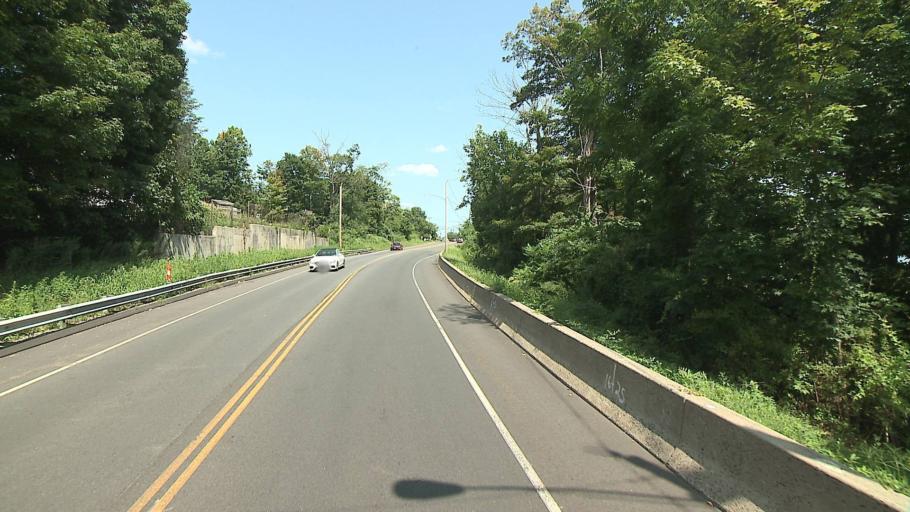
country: US
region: Connecticut
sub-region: New Haven County
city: City of Milford (balance)
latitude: 41.2403
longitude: -73.1059
